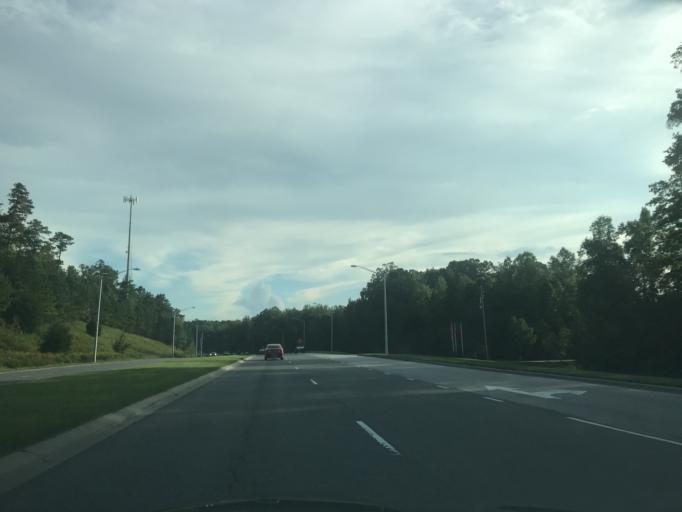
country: US
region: North Carolina
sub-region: Wake County
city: Green Level
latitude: 35.8583
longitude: -78.8944
